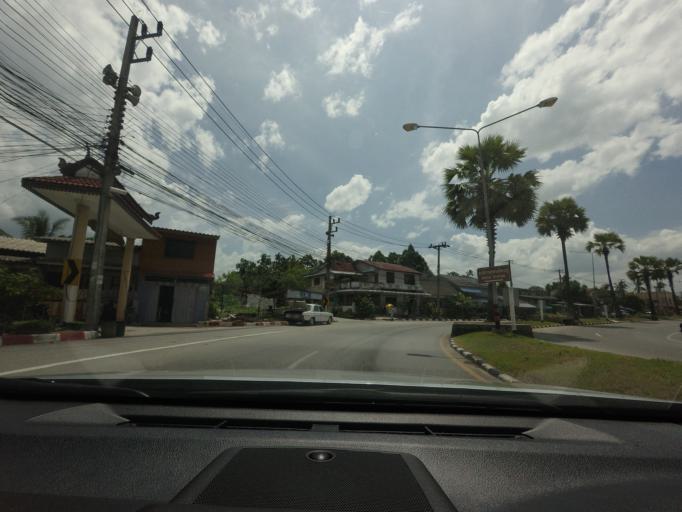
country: TH
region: Yala
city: Raman
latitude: 6.4545
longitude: 101.3463
